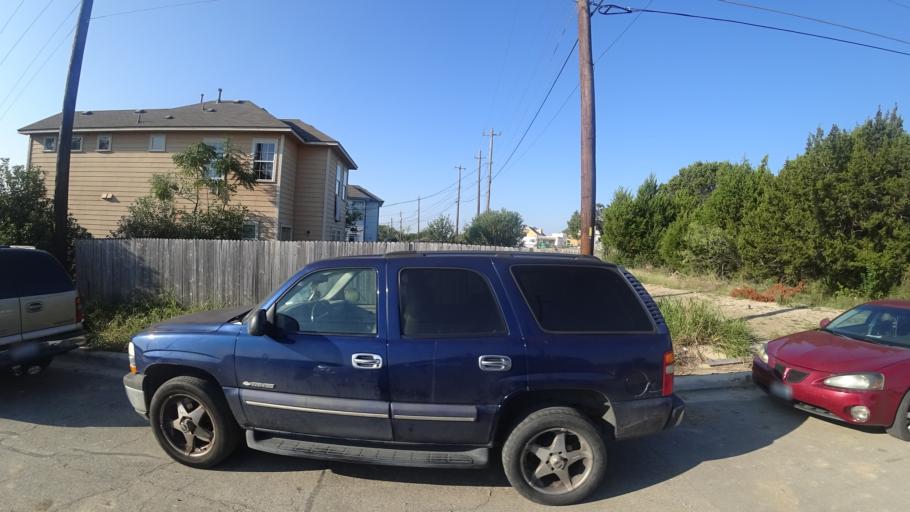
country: US
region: Texas
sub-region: Travis County
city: Austin
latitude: 30.3170
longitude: -97.6563
